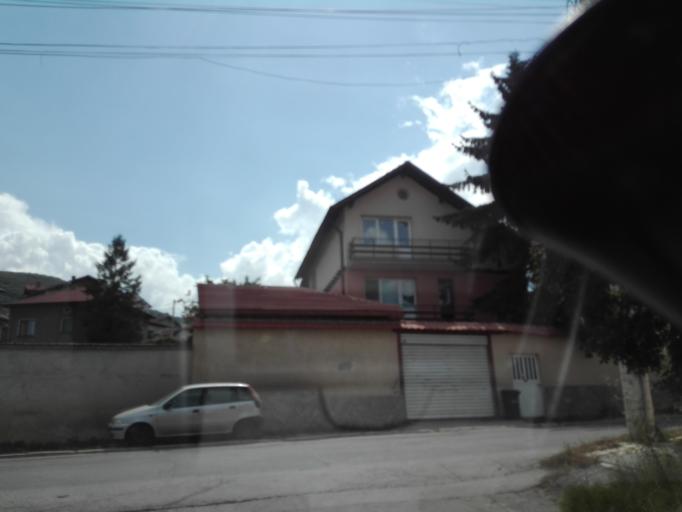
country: BG
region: Sofiya
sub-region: Obshtina Elin Pelin
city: Elin Pelin
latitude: 42.6018
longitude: 23.4839
